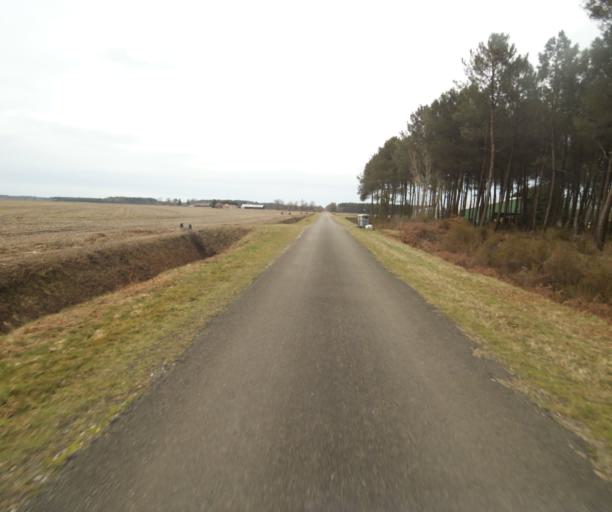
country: FR
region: Aquitaine
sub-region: Departement des Landes
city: Gabarret
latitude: 44.0343
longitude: -0.0671
